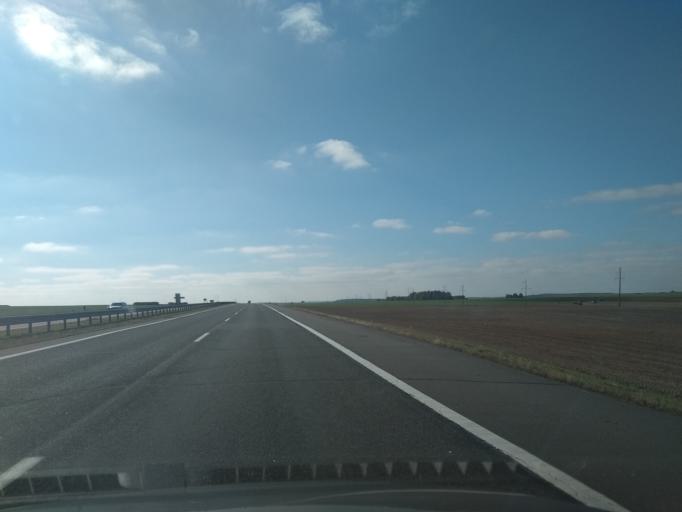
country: BY
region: Minsk
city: Snow
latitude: 53.3240
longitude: 26.4114
